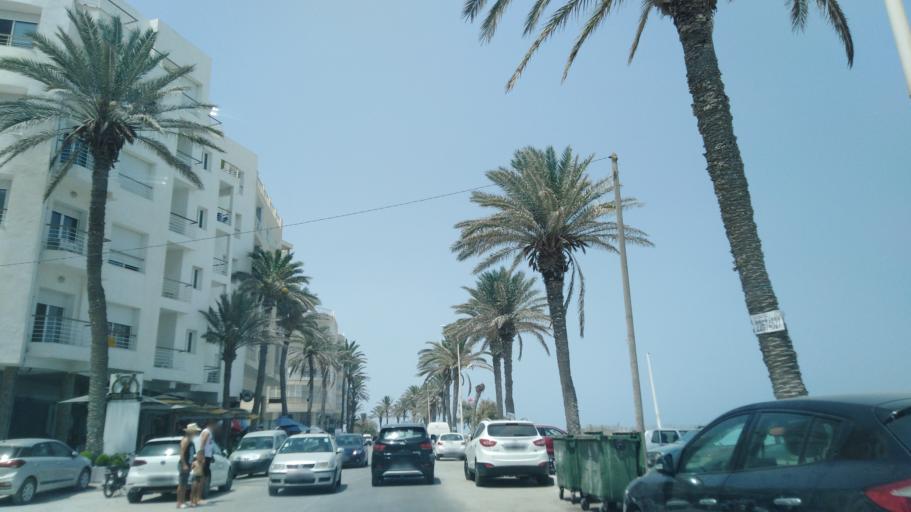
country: TN
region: Al Mahdiyah
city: Mahdia
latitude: 35.5215
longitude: 11.0422
